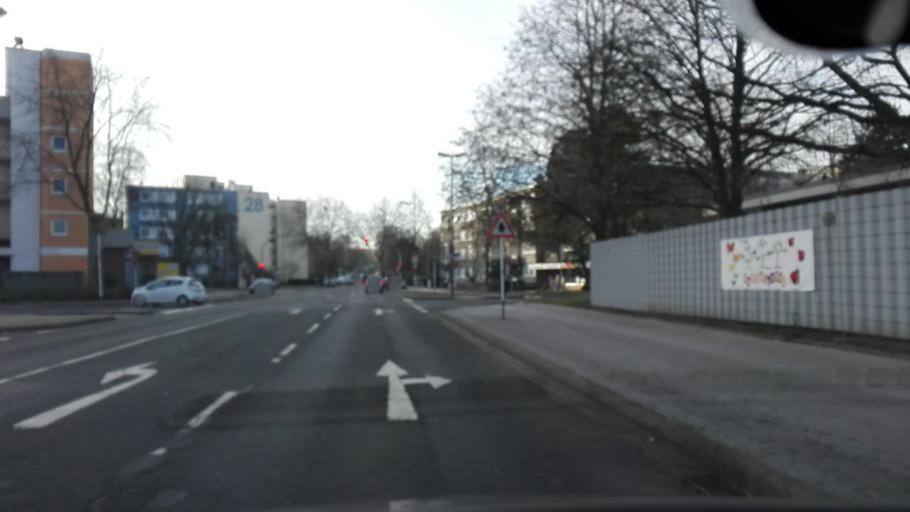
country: DE
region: North Rhine-Westphalia
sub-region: Regierungsbezirk Arnsberg
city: Dortmund
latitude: 51.5023
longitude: 7.4187
